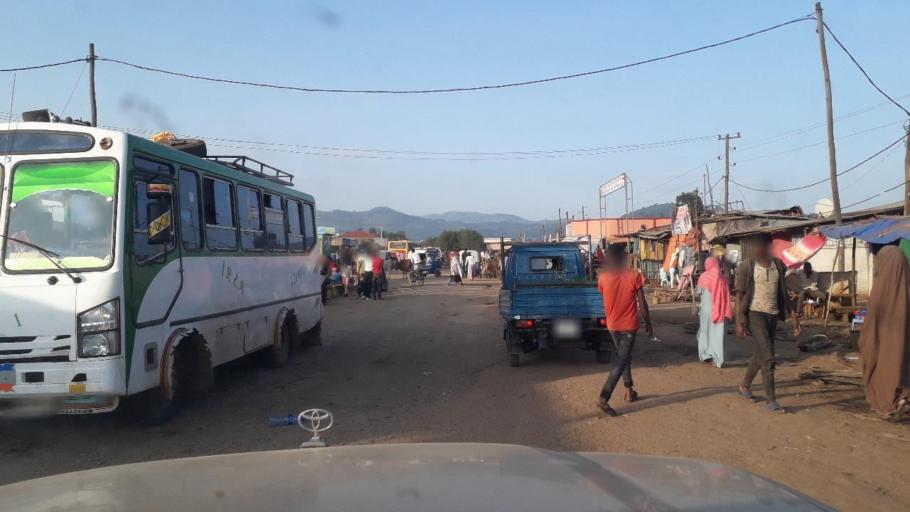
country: ET
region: Oromiya
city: Jima
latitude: 7.6439
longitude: 36.8434
